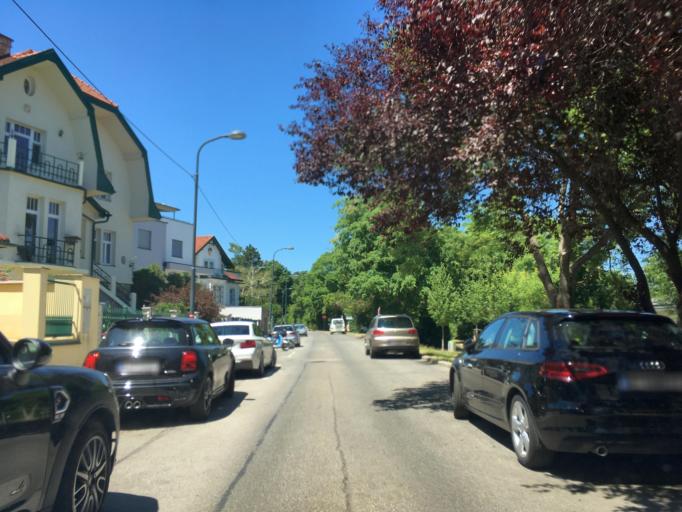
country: AT
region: Lower Austria
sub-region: Politischer Bezirk Modling
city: Perchtoldsdorf
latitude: 48.1940
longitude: 16.2579
